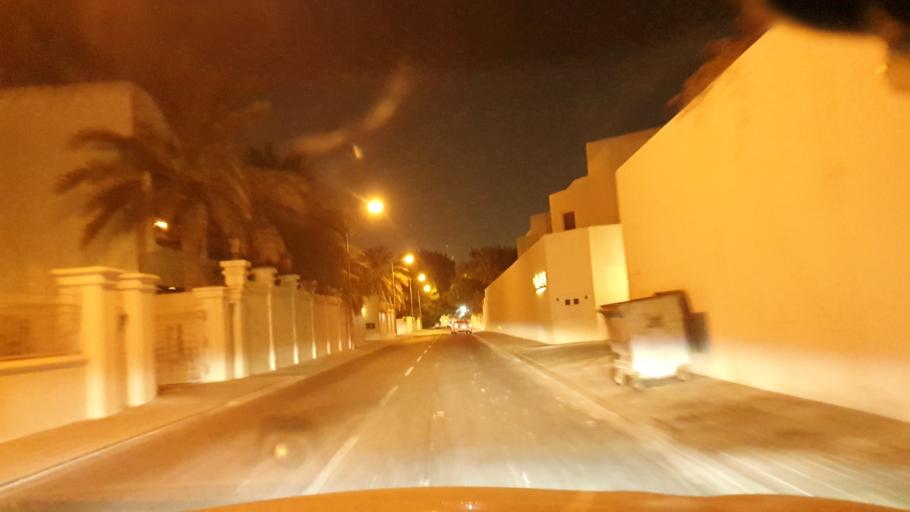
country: BH
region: Manama
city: Jidd Hafs
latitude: 26.1986
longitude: 50.4972
